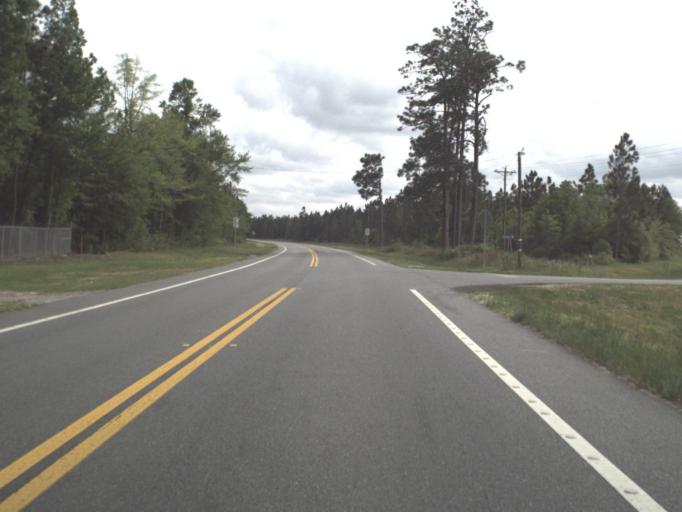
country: US
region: Alabama
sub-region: Escambia County
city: East Brewton
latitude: 30.9726
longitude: -87.0466
